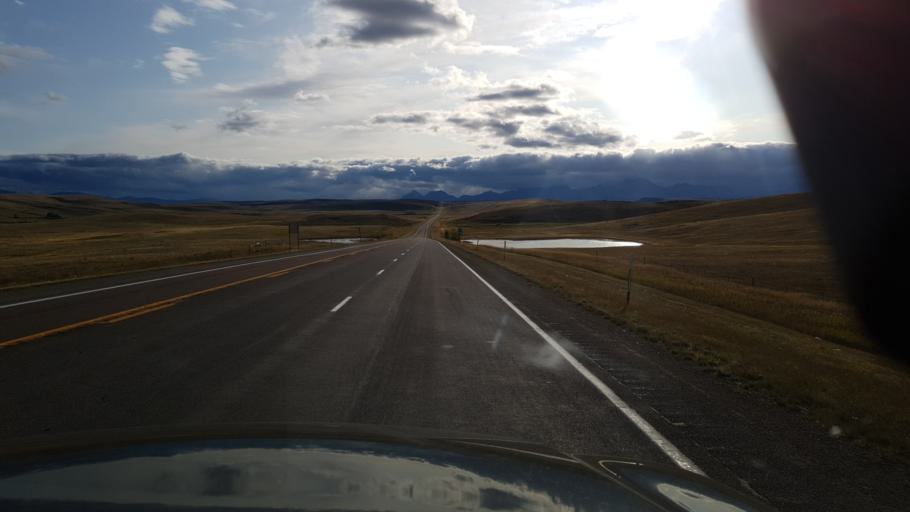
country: US
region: Montana
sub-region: Glacier County
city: South Browning
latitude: 48.5395
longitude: -113.0380
